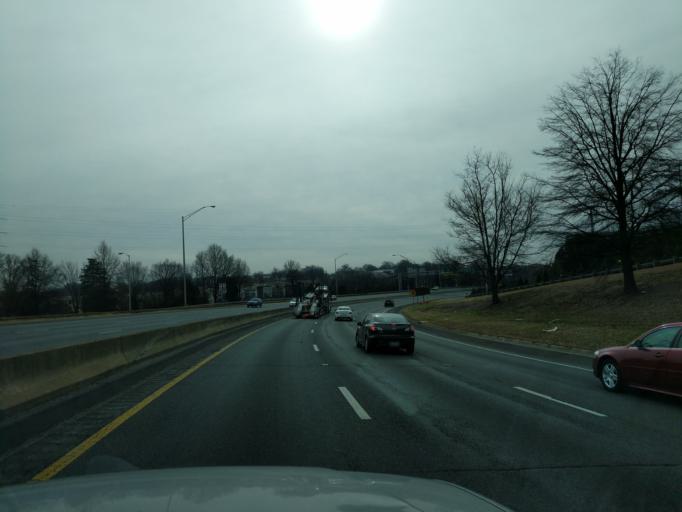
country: US
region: North Carolina
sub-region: Mecklenburg County
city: Charlotte
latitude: 35.2279
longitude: -80.8291
